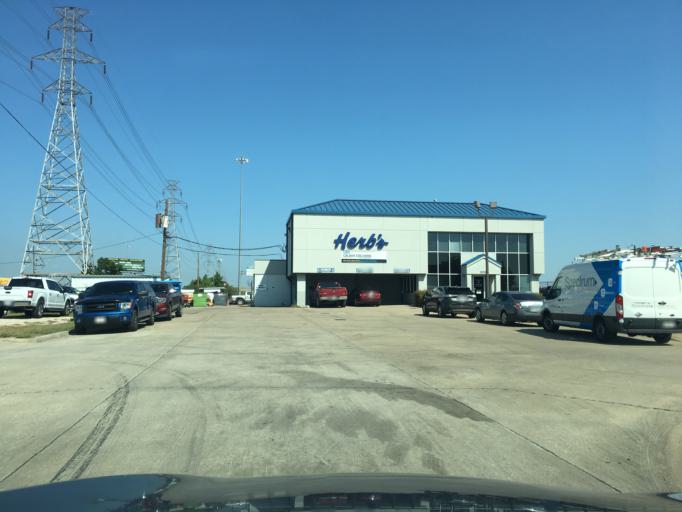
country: US
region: Texas
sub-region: Dallas County
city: Garland
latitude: 32.8686
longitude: -96.6708
